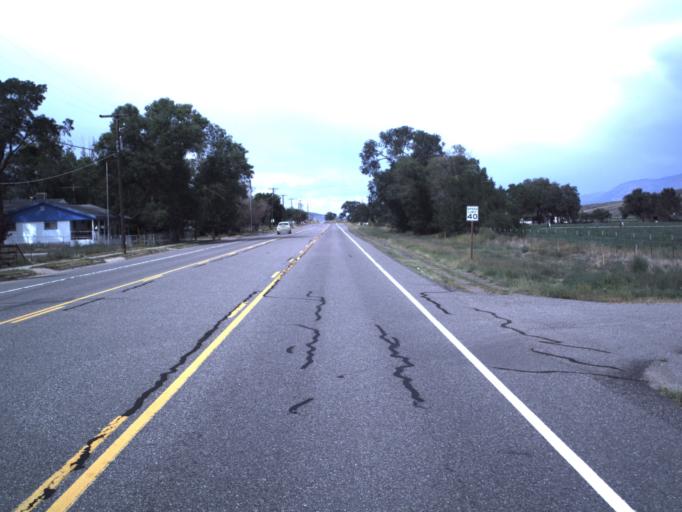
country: US
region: Utah
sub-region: Piute County
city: Junction
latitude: 38.2401
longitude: -112.2200
